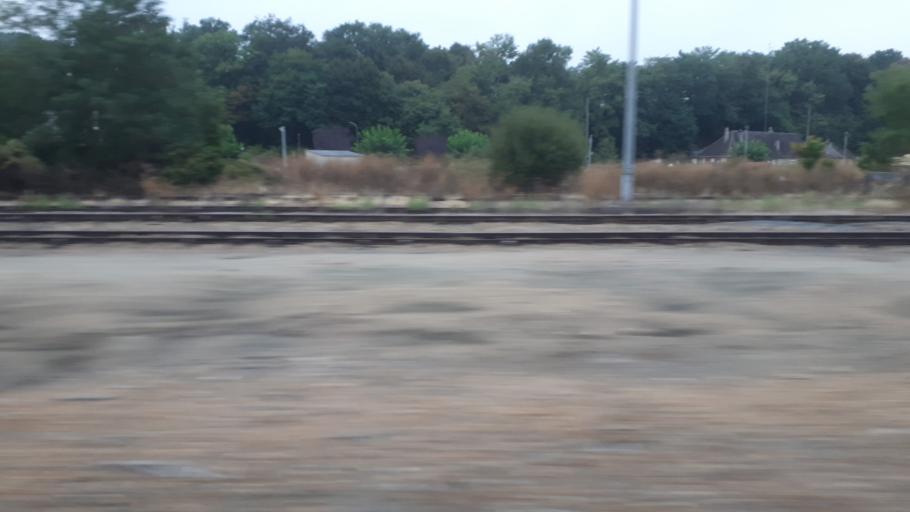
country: FR
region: Centre
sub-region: Departement d'Indre-et-Loire
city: Chateau-Renault
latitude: 47.5852
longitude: 0.8992
